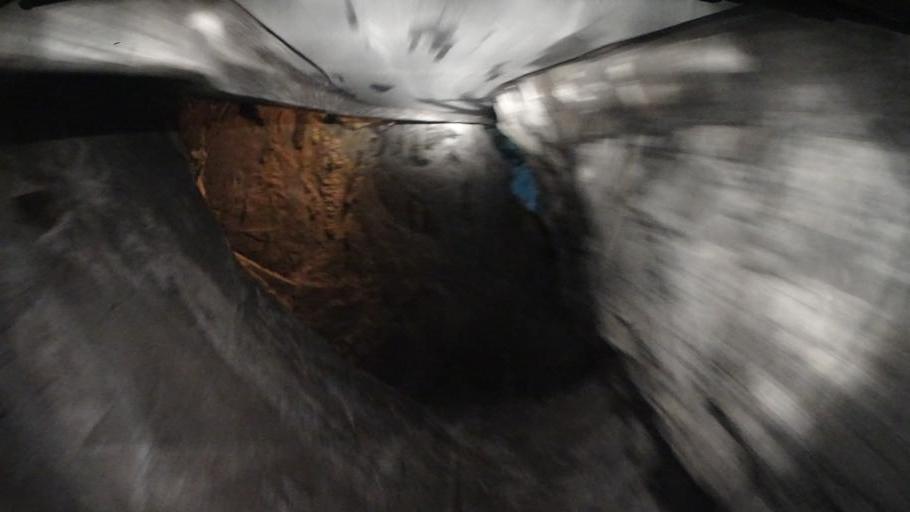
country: ES
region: Asturias
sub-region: Province of Asturias
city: Ribadesella
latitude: 43.4352
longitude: -5.0728
